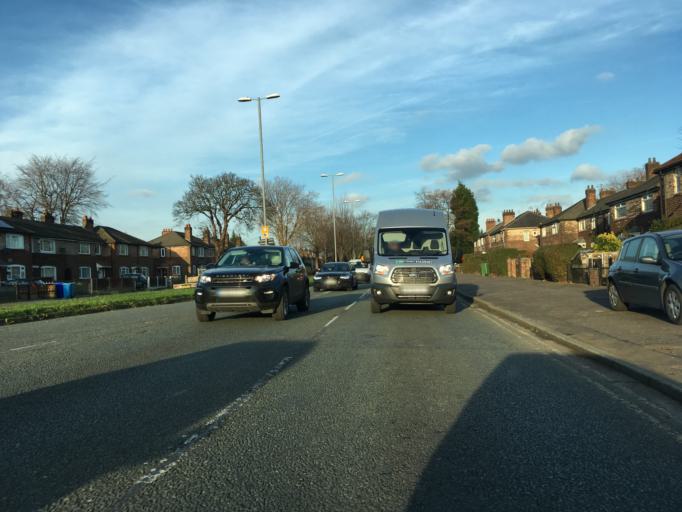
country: GB
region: England
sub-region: Manchester
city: Burnage
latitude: 53.4214
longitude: -2.2130
